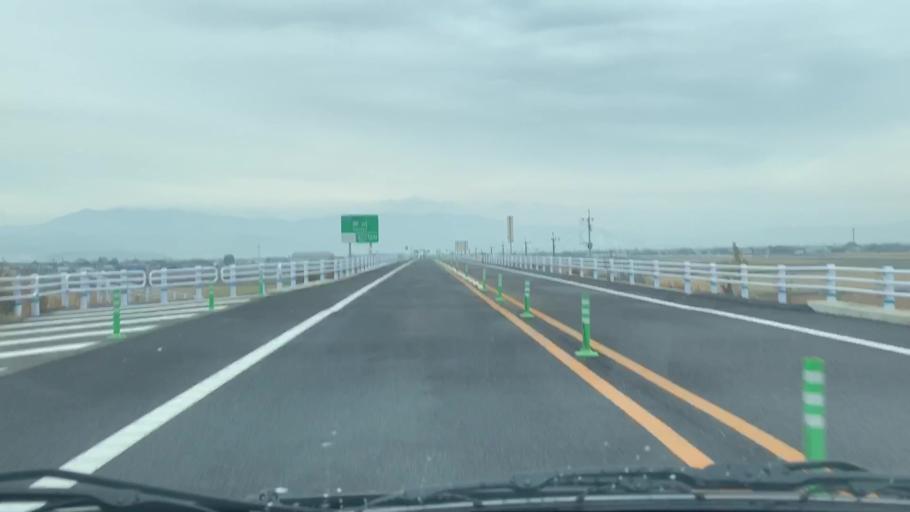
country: JP
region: Saga Prefecture
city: Saga-shi
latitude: 33.2089
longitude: 130.2150
